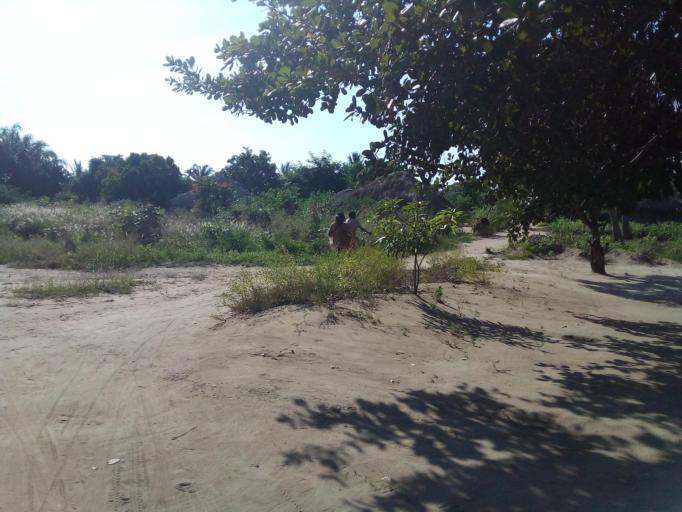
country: MZ
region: Zambezia
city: Quelimane
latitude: -17.5550
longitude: 36.7009
